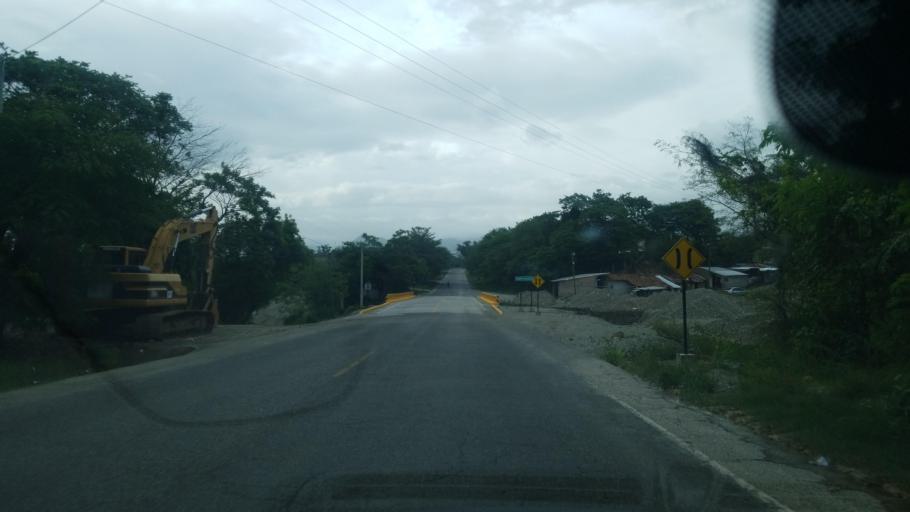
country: HN
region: Ocotepeque
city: Santa Lucia
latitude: 14.4126
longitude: -89.1947
